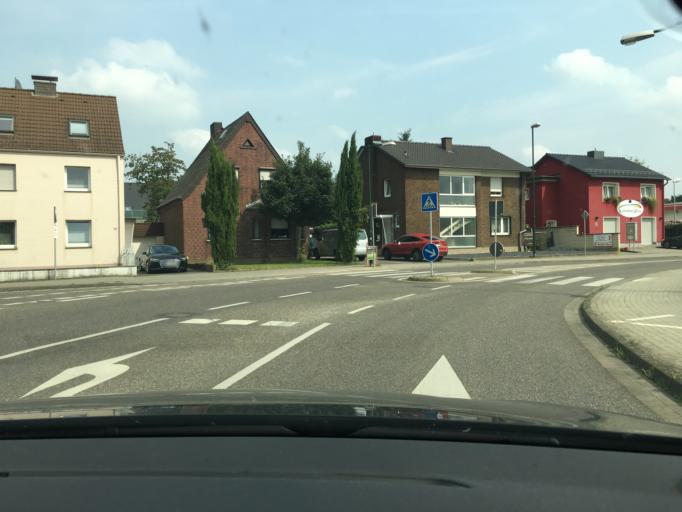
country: DE
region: North Rhine-Westphalia
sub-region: Regierungsbezirk Koln
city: Merzenich
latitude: 50.8619
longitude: 6.5775
